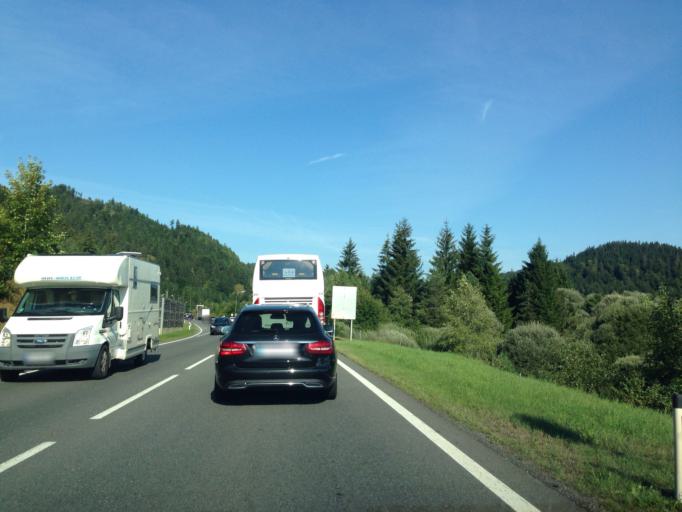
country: AT
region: Tyrol
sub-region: Politischer Bezirk Reutte
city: Musau
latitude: 47.5379
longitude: 10.6717
